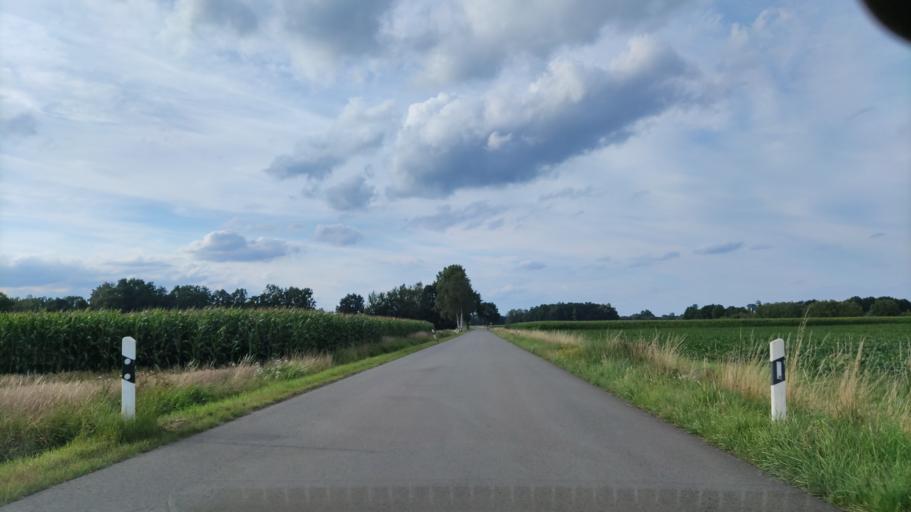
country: DE
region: Lower Saxony
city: Dannenberg
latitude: 53.0841
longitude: 11.1031
